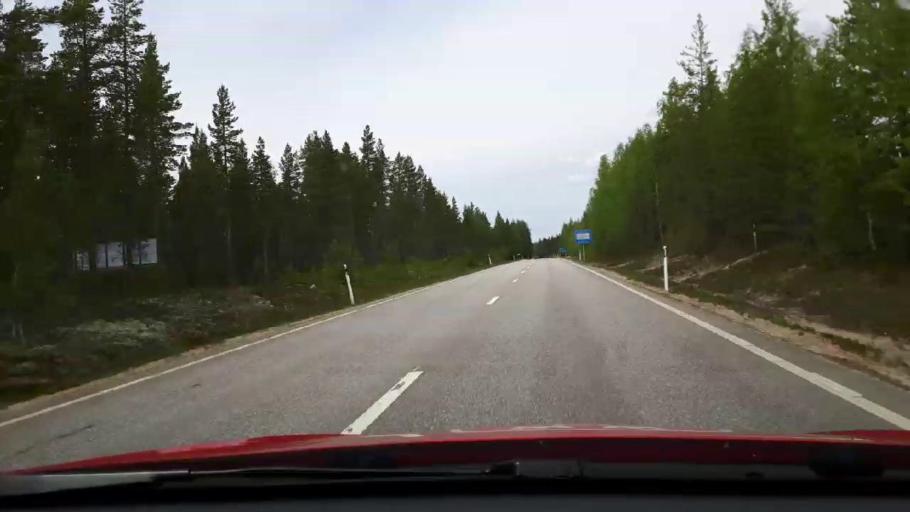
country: SE
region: Jaemtland
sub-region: Harjedalens Kommun
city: Sveg
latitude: 62.1164
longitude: 14.1750
